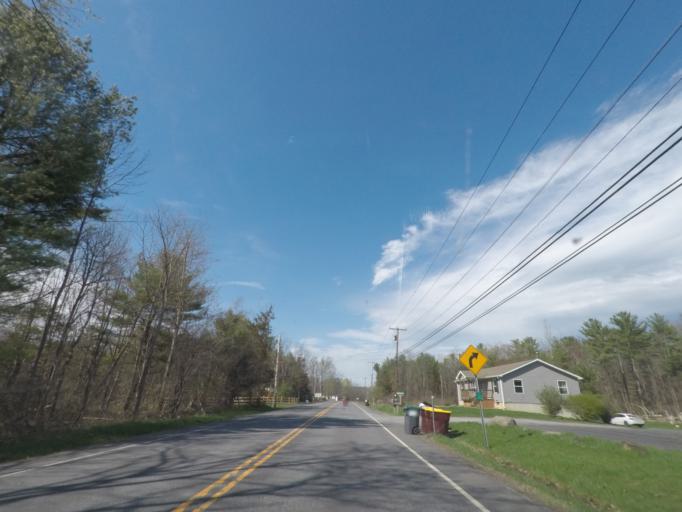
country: US
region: New York
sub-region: Greene County
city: Cairo
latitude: 42.3757
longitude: -74.0353
